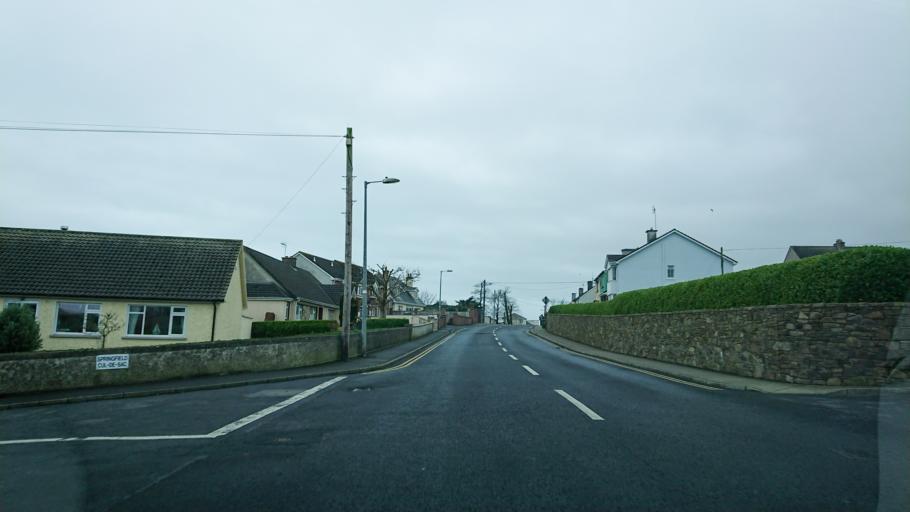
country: IE
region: Munster
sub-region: Waterford
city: Tra Mhor
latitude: 52.1682
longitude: -7.1485
